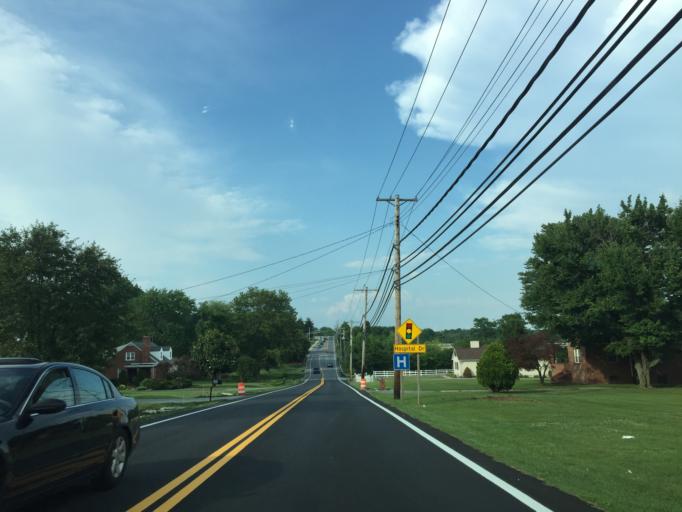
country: US
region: Maryland
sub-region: Baltimore County
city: Rossville
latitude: 39.3443
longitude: -76.4765
